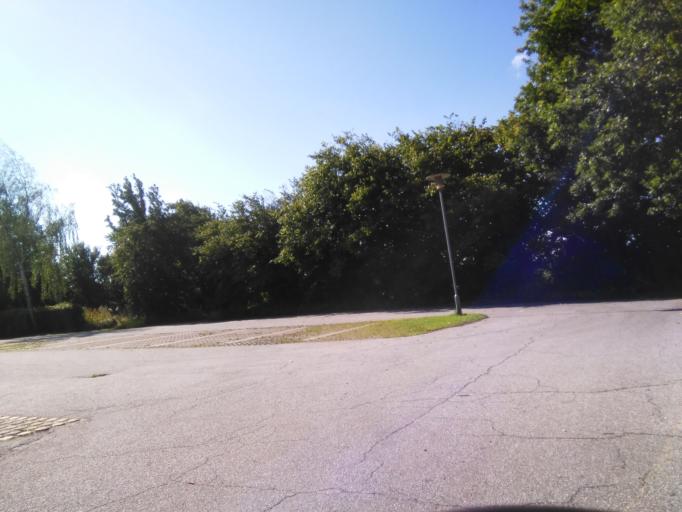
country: DK
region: Central Jutland
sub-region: Arhus Kommune
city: Beder
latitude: 56.0533
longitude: 10.2087
